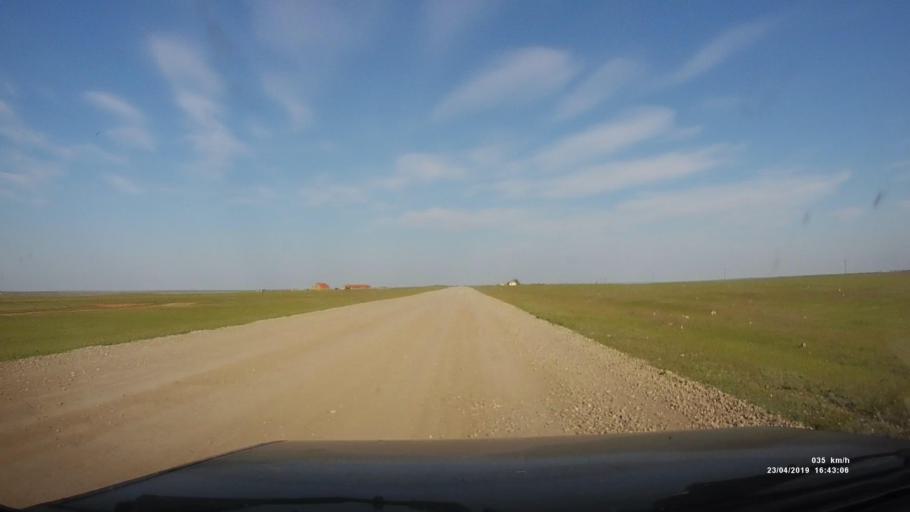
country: RU
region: Kalmykiya
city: Priyutnoye
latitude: 46.3478
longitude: 43.2019
